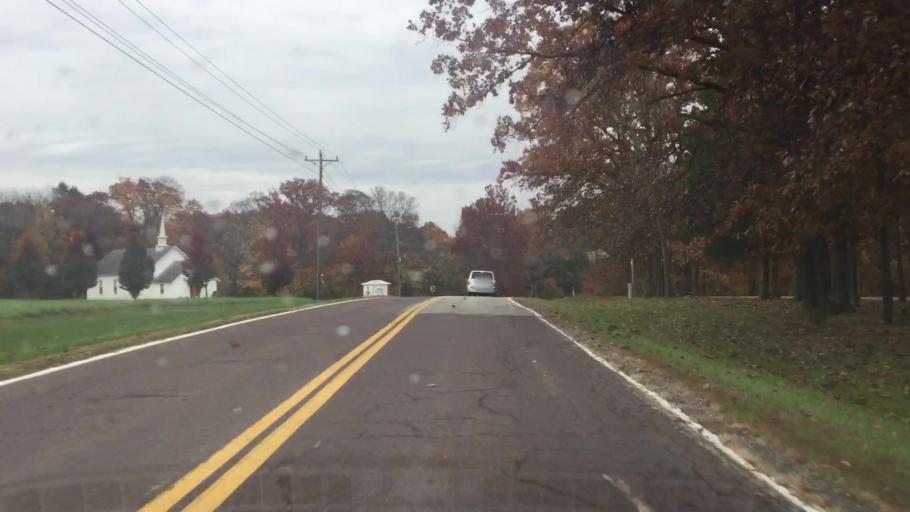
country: US
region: Missouri
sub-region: Callaway County
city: Fulton
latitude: 38.7872
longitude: -91.7904
